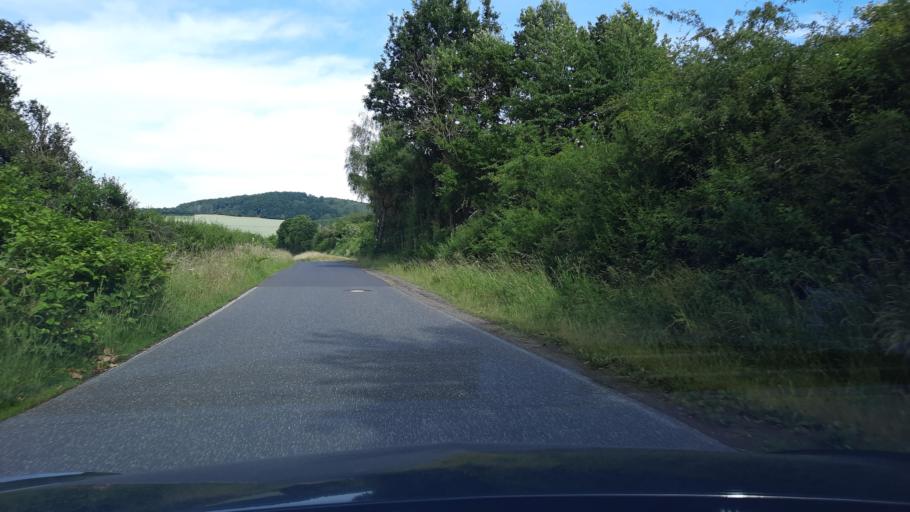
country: DE
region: Rheinland-Pfalz
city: Brenk
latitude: 50.4192
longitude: 7.1643
